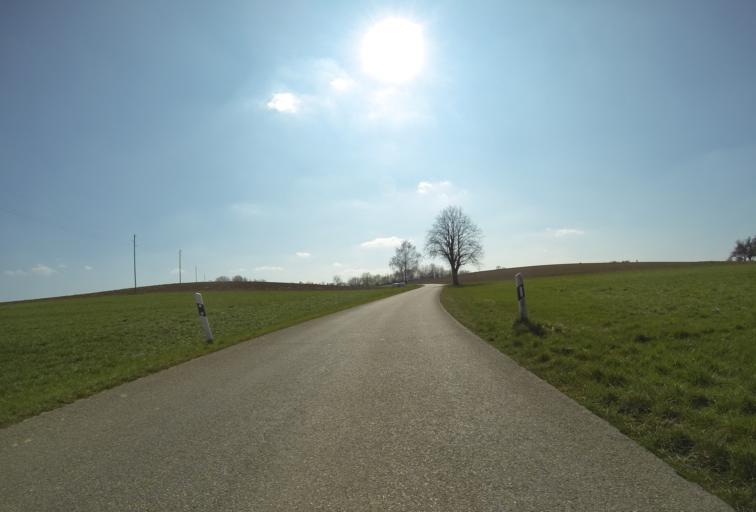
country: DE
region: Baden-Wuerttemberg
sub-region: Tuebingen Region
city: Huttisheim
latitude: 48.2911
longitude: 9.9480
